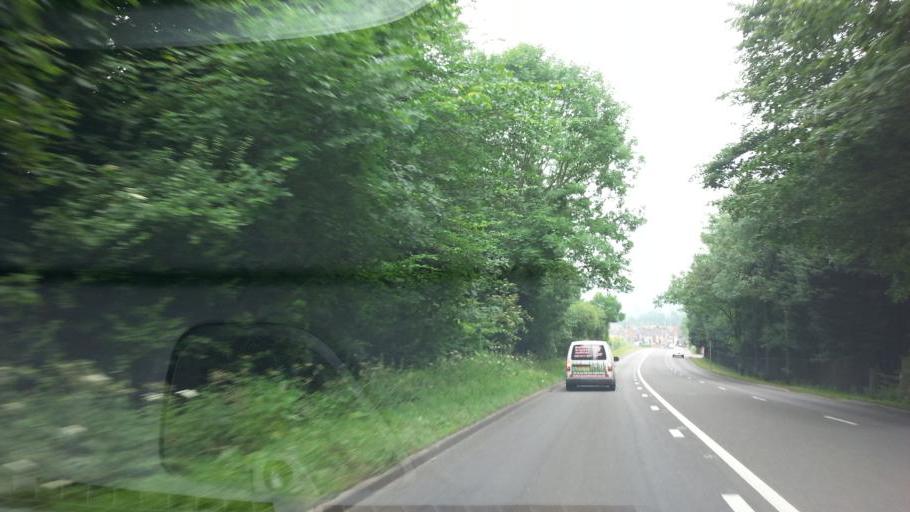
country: GB
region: England
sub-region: Staffordshire
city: Barton under Needwood
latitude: 52.8501
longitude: -1.7732
